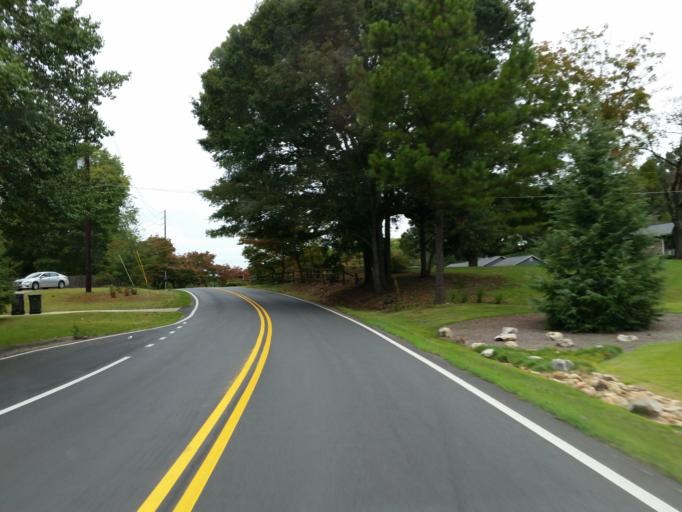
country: US
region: Georgia
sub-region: Cherokee County
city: Woodstock
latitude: 34.0490
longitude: -84.5226
